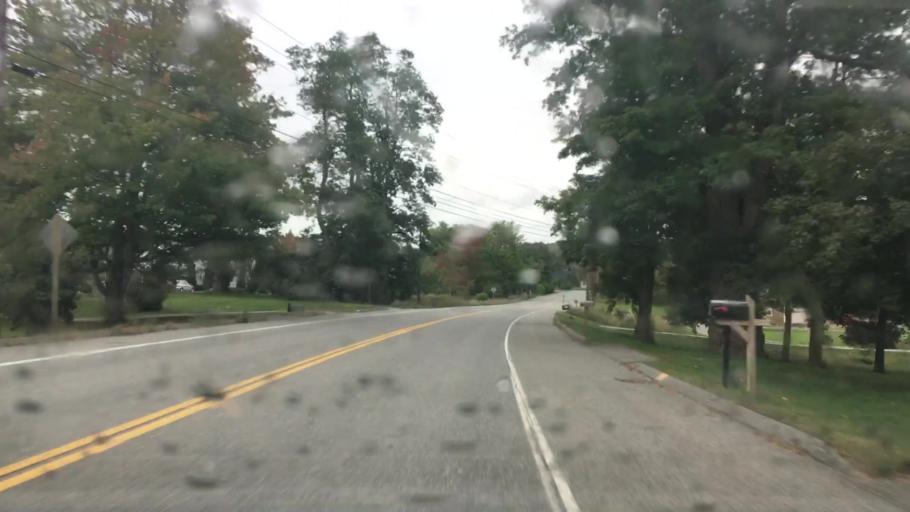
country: US
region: Maine
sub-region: Penobscot County
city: Orrington
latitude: 44.7219
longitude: -68.8261
